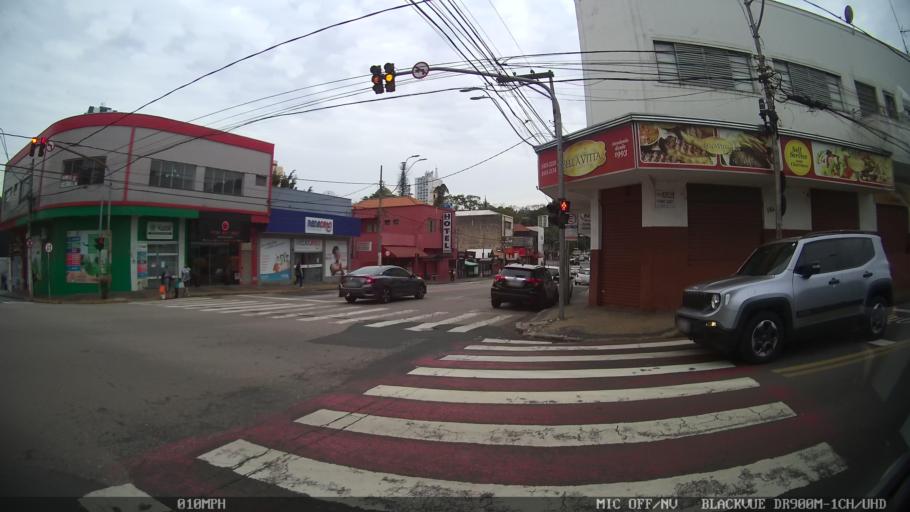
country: BR
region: Sao Paulo
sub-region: Americana
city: Americana
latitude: -22.7417
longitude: -47.3293
